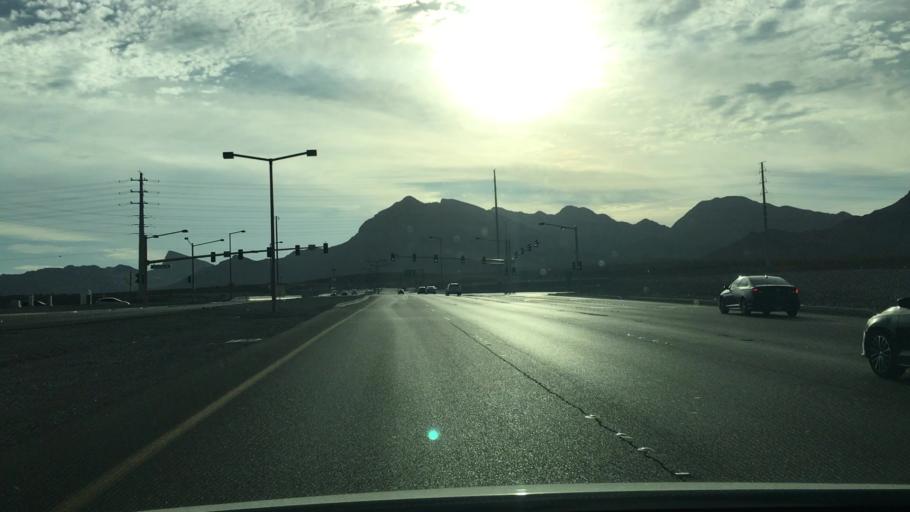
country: US
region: Nevada
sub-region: Clark County
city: Summerlin South
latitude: 36.1915
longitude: -115.3403
